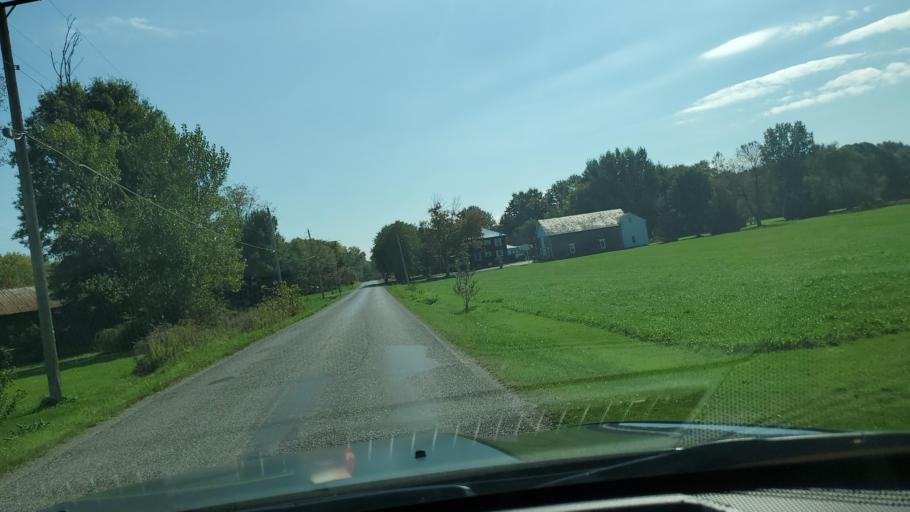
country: US
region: Ohio
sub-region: Trumbull County
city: Cortland
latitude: 41.4348
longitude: -80.6101
